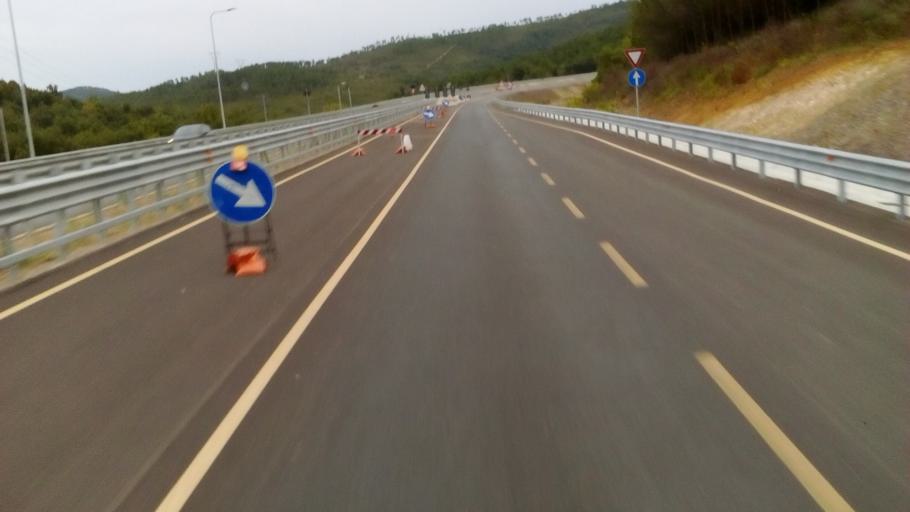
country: IT
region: Tuscany
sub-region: Provincia di Grosseto
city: Civitella Marittima
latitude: 43.0307
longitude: 11.2771
